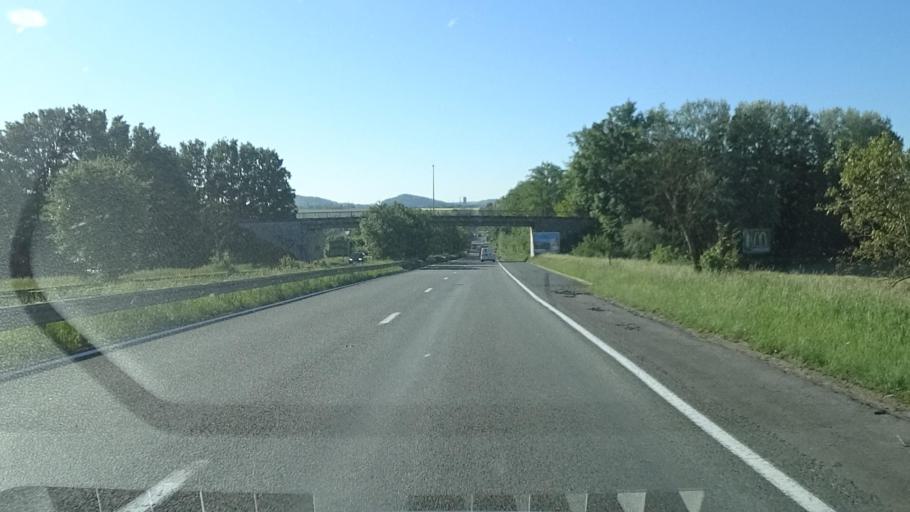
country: BE
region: Wallonia
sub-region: Province du Hainaut
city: Binche
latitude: 50.4572
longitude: 4.1488
